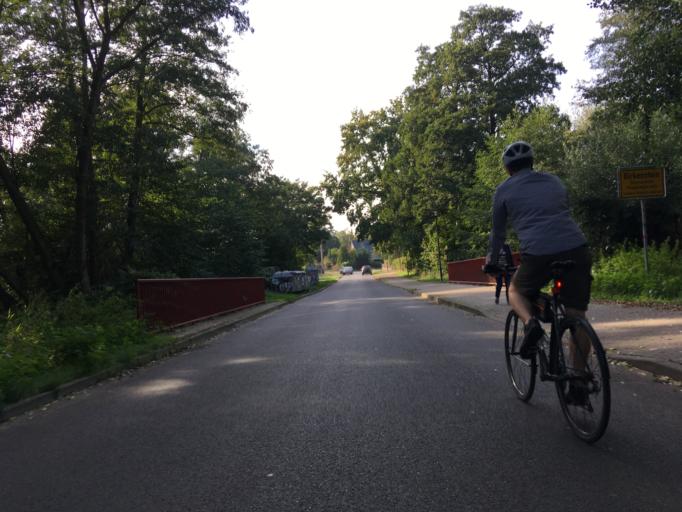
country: DE
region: Brandenburg
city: Hoppegarten
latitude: 52.5177
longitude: 13.6612
